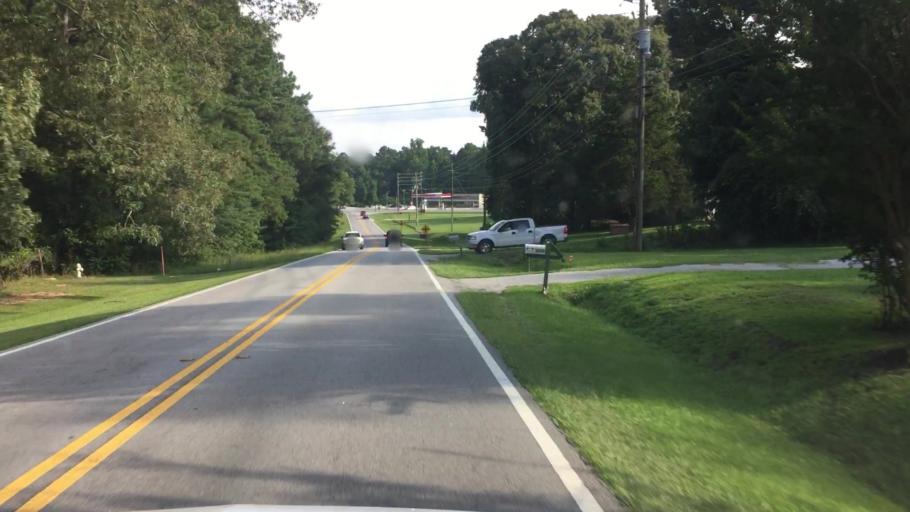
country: US
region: Georgia
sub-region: DeKalb County
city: Pine Mountain
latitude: 33.6102
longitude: -84.1370
